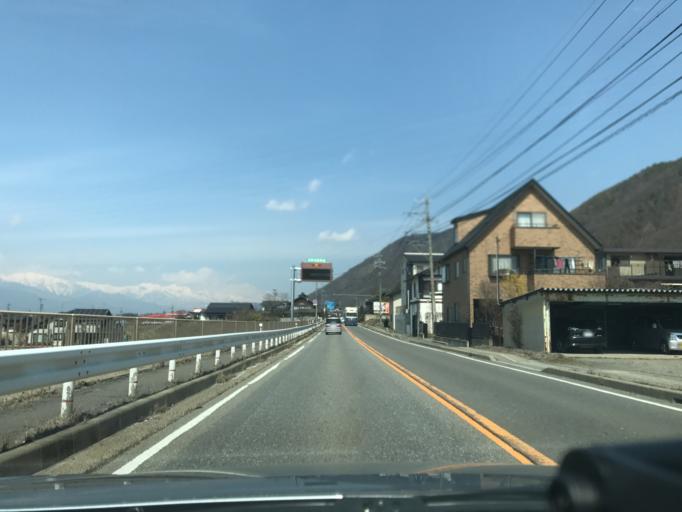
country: JP
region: Nagano
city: Toyoshina
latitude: 36.2983
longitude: 137.9409
